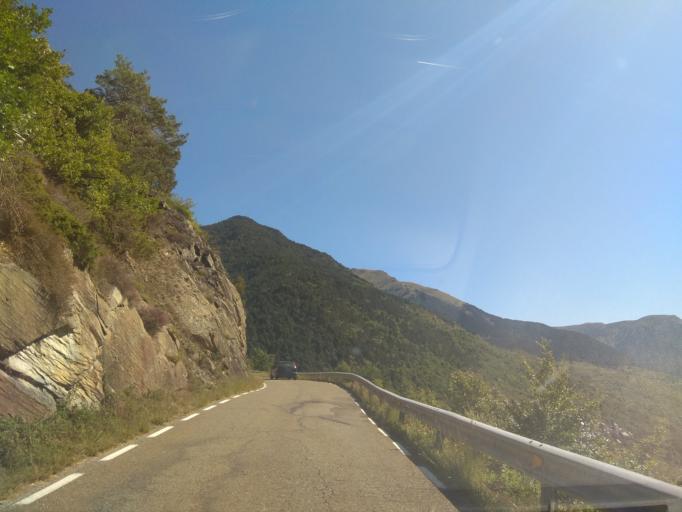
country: ES
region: Catalonia
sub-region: Provincia de Lleida
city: Vielha
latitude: 42.7402
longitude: 0.7505
